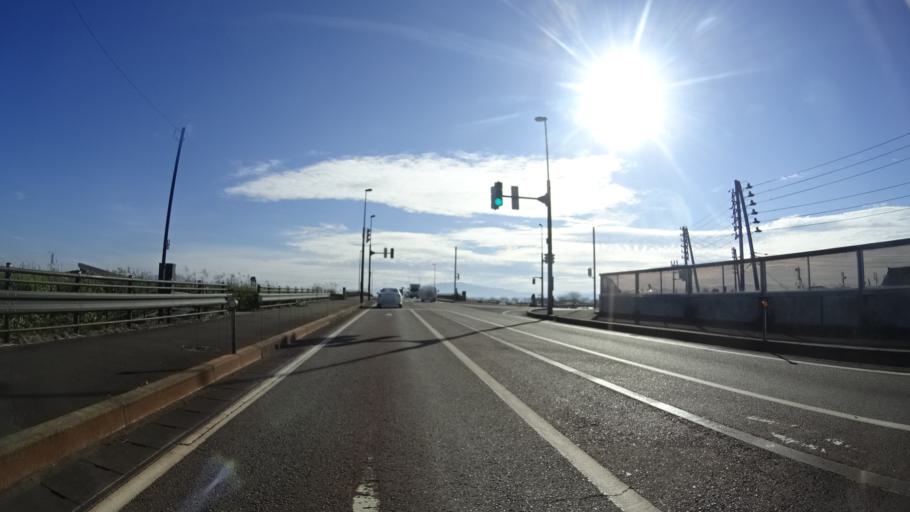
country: JP
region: Niigata
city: Mitsuke
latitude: 37.5461
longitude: 138.8808
